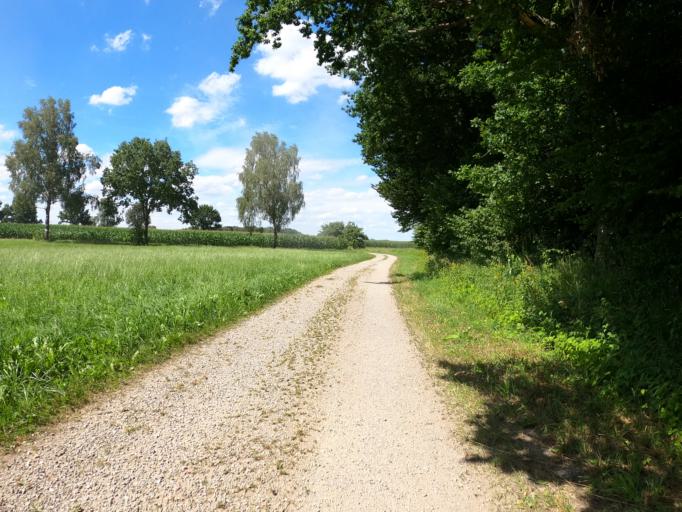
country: DE
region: Bavaria
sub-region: Swabia
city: Leipheim
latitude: 48.4211
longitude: 10.2038
